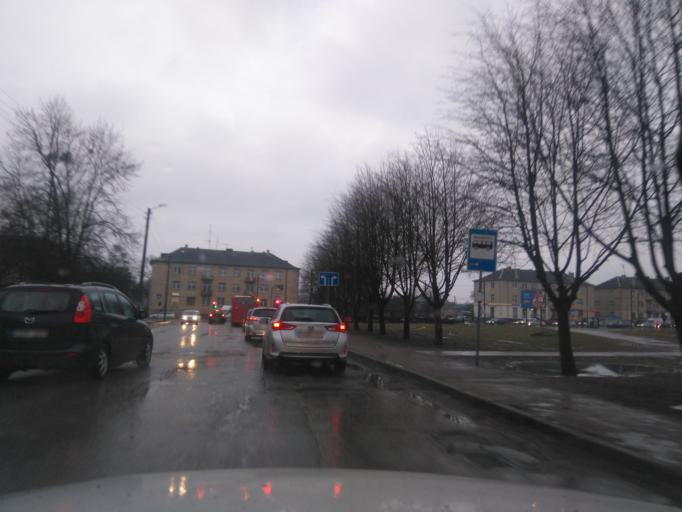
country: LT
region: Kauno apskritis
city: Dainava (Kaunas)
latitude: 54.8968
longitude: 23.9565
